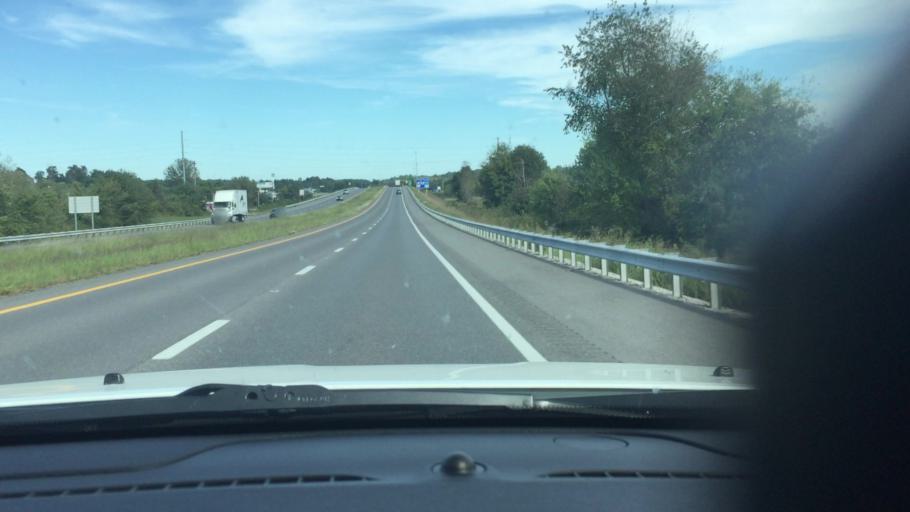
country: US
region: Kentucky
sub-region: Caldwell County
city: Princeton
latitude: 37.1198
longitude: -87.9062
